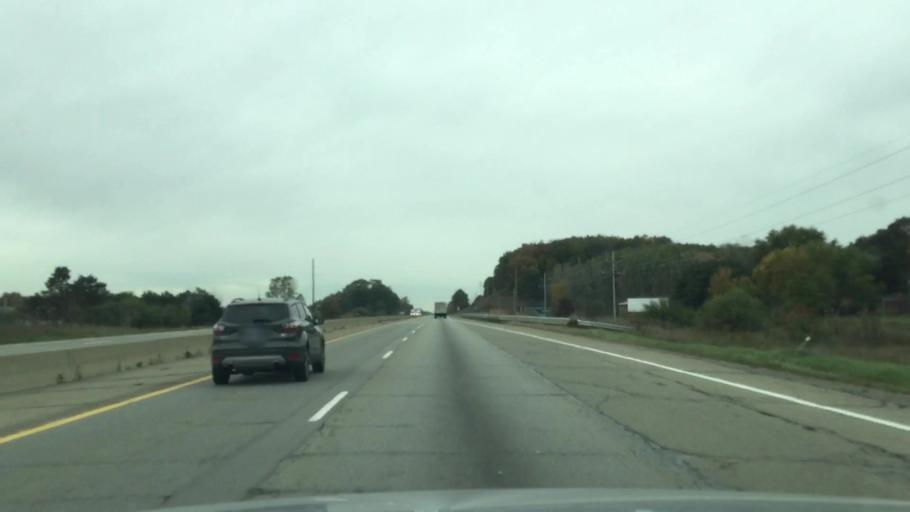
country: US
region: Michigan
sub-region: Jackson County
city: Spring Arbor
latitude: 42.2692
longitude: -84.5426
